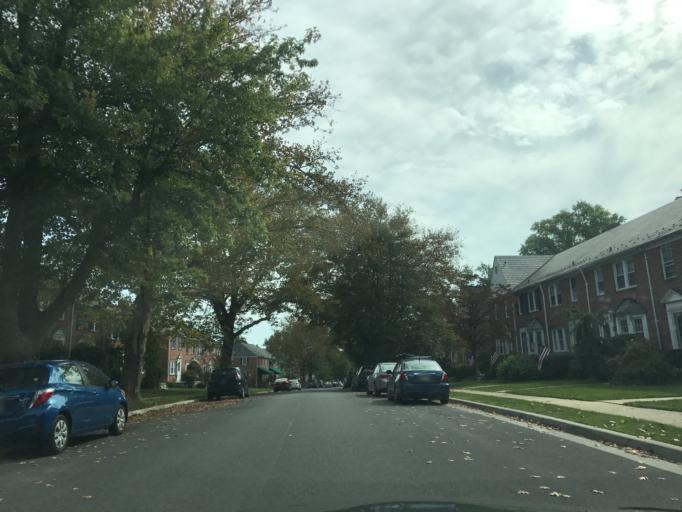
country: US
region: Maryland
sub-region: Baltimore County
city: Towson
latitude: 39.3758
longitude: -76.6144
